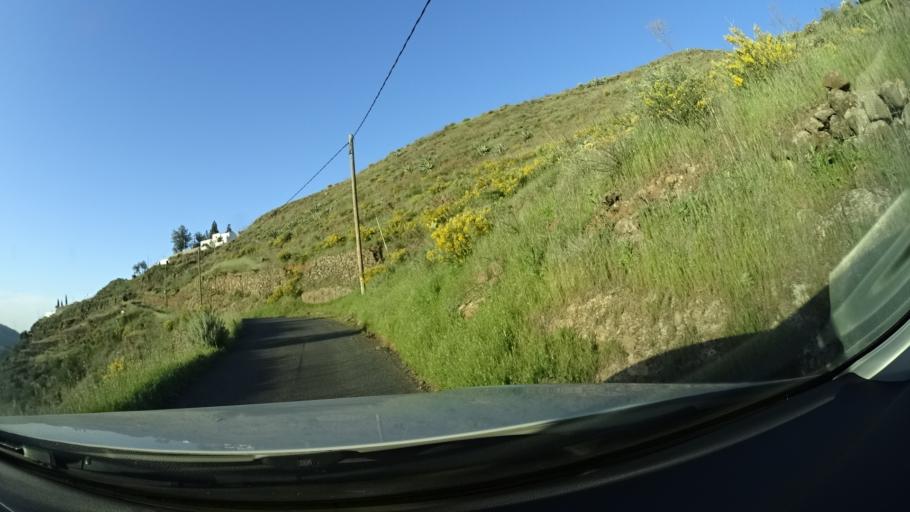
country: ES
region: Canary Islands
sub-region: Provincia de Las Palmas
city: Artenara
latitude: 28.0366
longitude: -15.6460
